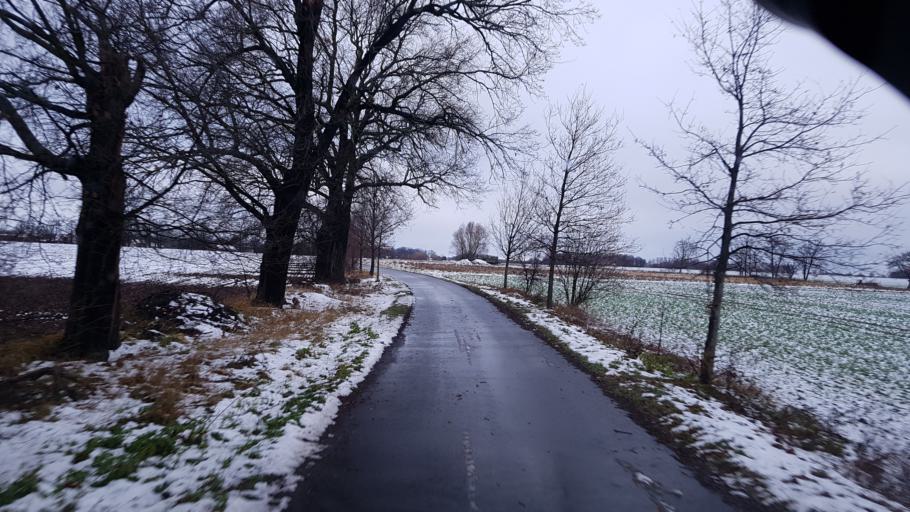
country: DE
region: Brandenburg
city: Crinitz
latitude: 51.7857
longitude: 13.7493
